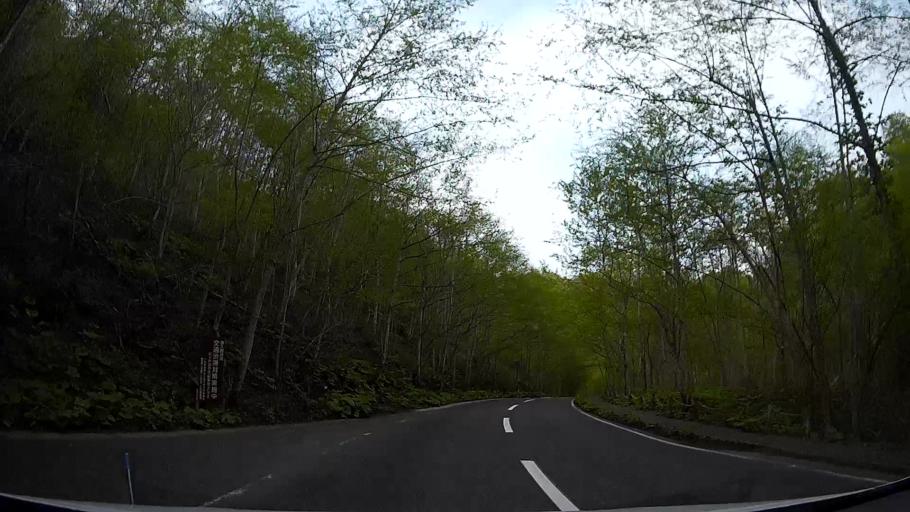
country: JP
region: Aomori
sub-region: Aomori Shi
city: Furudate
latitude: 40.5279
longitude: 140.9740
